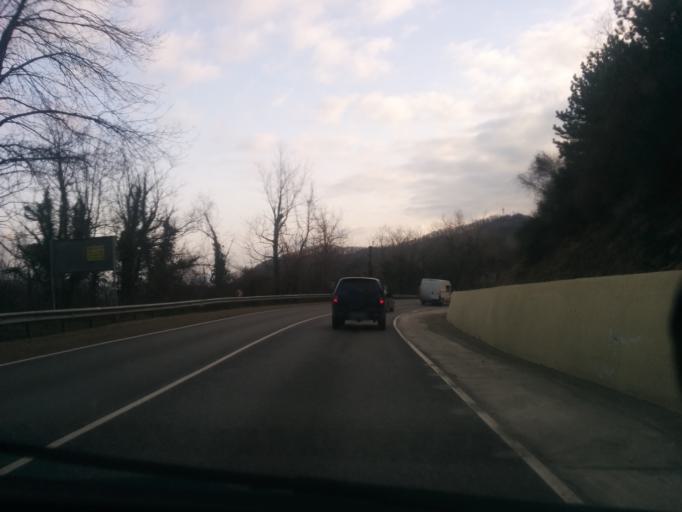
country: RU
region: Krasnodarskiy
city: Agoy
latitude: 44.1263
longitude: 39.0482
